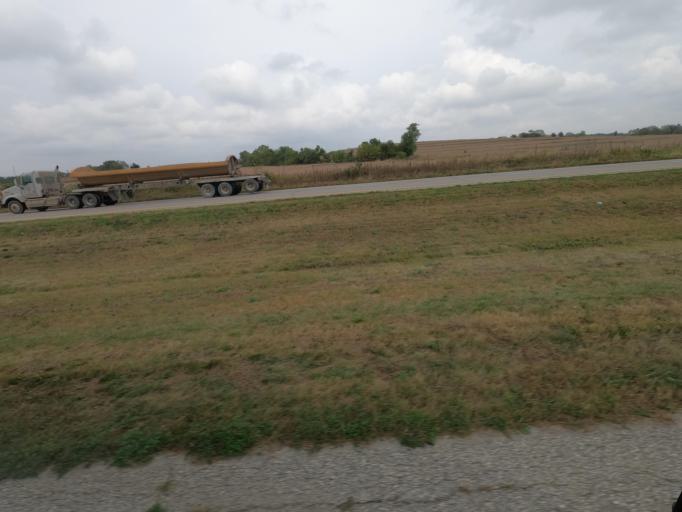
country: US
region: Iowa
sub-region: Wapello County
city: Eddyville
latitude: 41.1083
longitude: -92.5357
